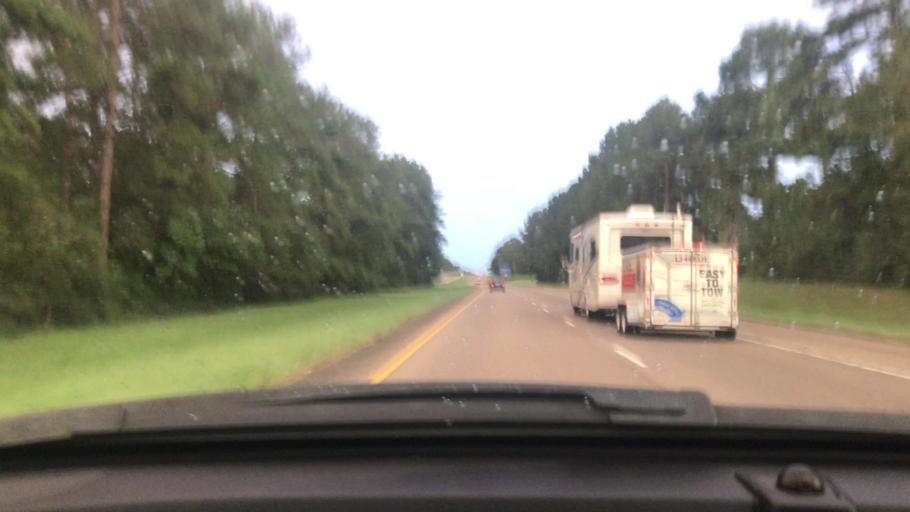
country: US
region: Louisiana
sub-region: Tangipahoa Parish
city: Roseland
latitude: 30.7924
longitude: -90.5333
